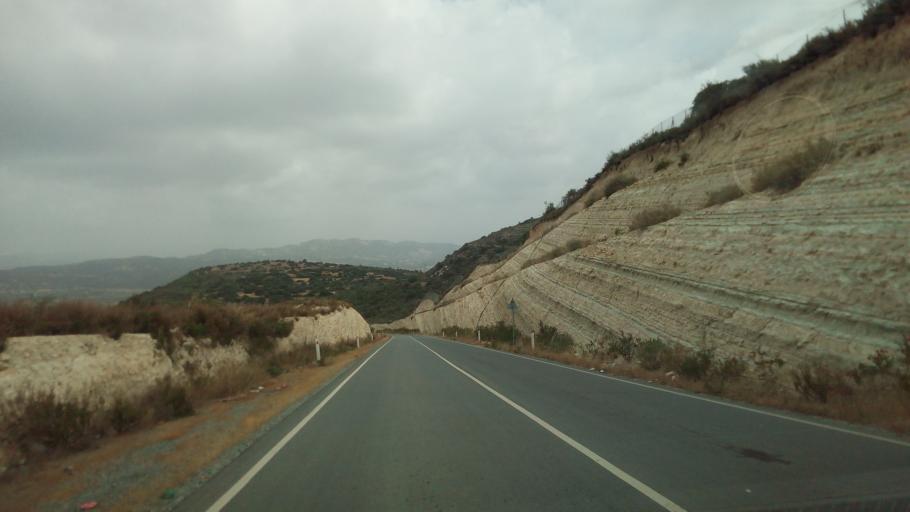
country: CY
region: Limassol
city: Pano Polemidia
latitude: 34.7449
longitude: 32.9538
